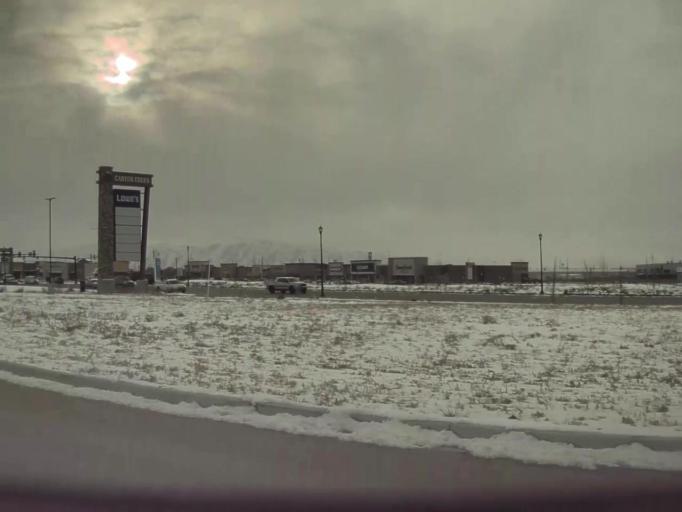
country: US
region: Utah
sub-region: Utah County
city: Spanish Fork
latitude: 40.1281
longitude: -111.6366
